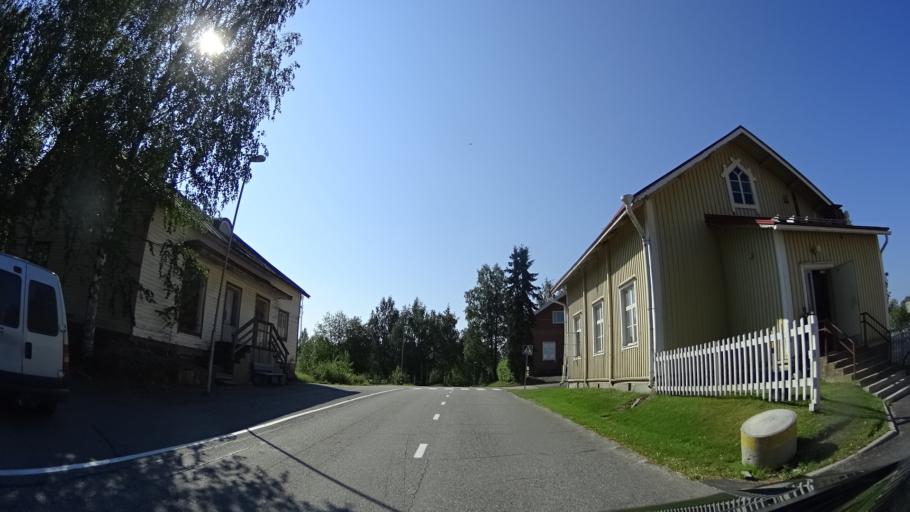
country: FI
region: North Karelia
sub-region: Joensuu
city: Juuka
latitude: 63.2415
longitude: 29.2502
